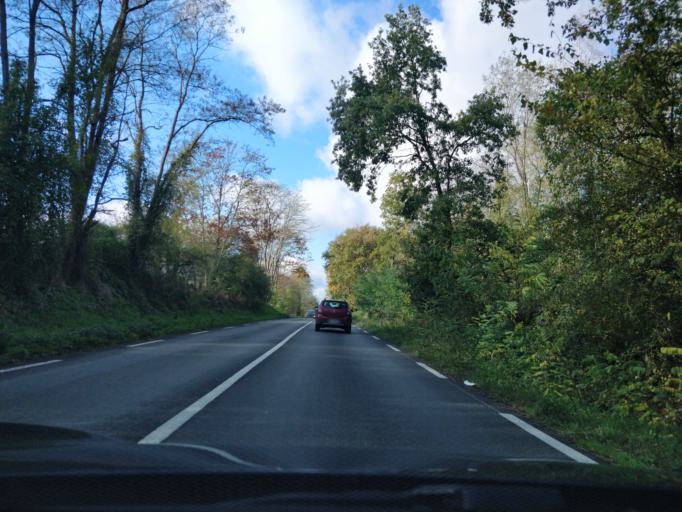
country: FR
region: Ile-de-France
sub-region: Departement de l'Essonne
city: Bruyeres-le-Chatel
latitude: 48.6098
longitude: 2.1810
